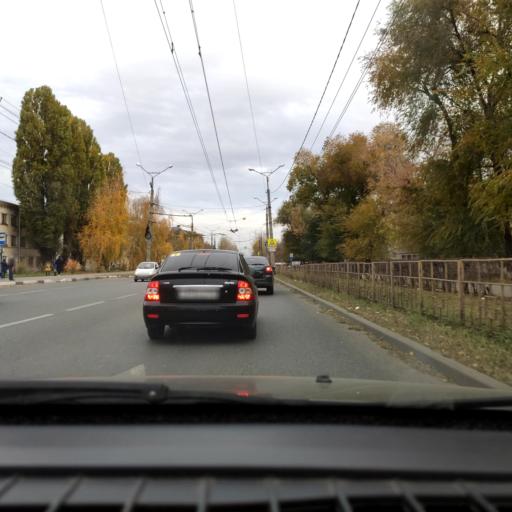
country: RU
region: Samara
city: Tol'yatti
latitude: 53.5288
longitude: 49.4128
